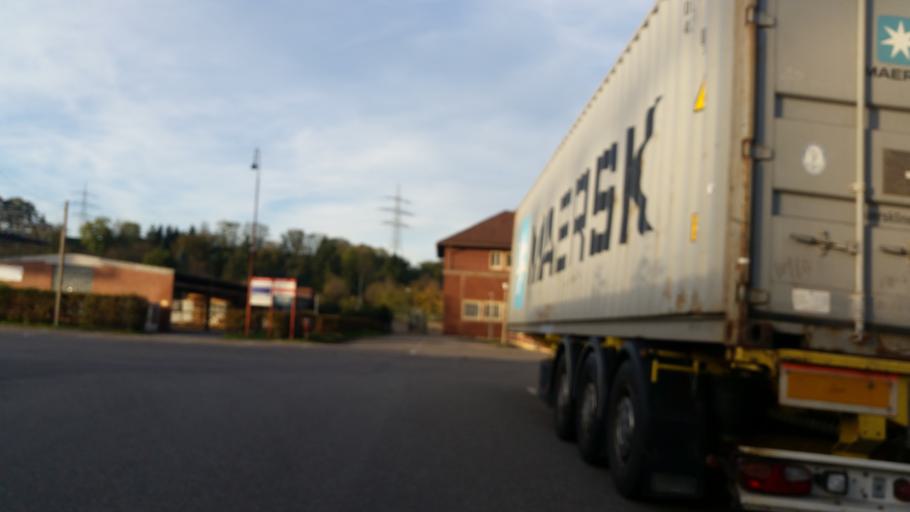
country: DE
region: Baden-Wuerttemberg
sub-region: Regierungsbezirk Stuttgart
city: Benningen am Neckar
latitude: 48.9276
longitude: 9.2373
